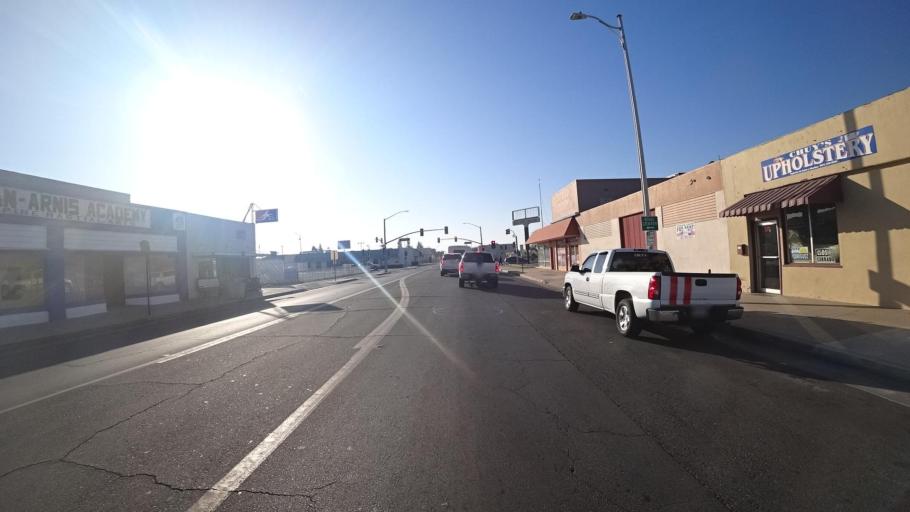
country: US
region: California
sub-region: Kern County
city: Delano
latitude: 35.7709
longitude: -119.2475
